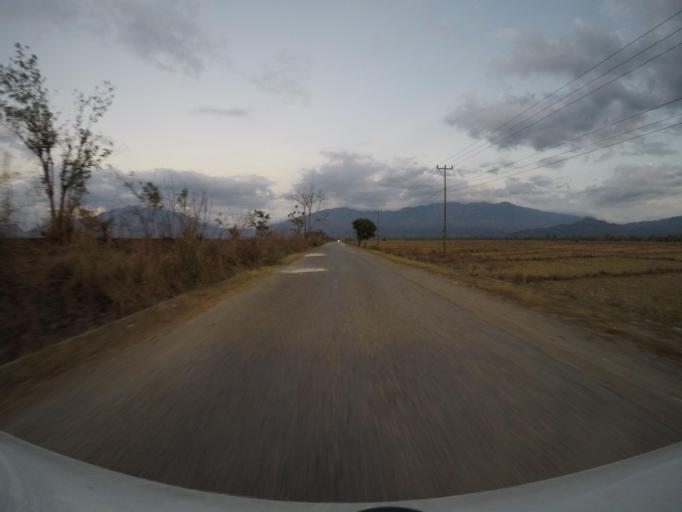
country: TL
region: Bobonaro
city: Maliana
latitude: -8.9833
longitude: 125.1567
